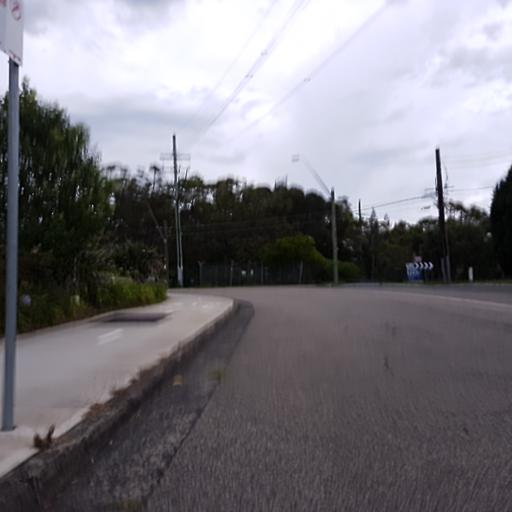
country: AU
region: New South Wales
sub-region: Warringah
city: Allambie Heights
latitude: -33.7566
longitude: 151.2448
